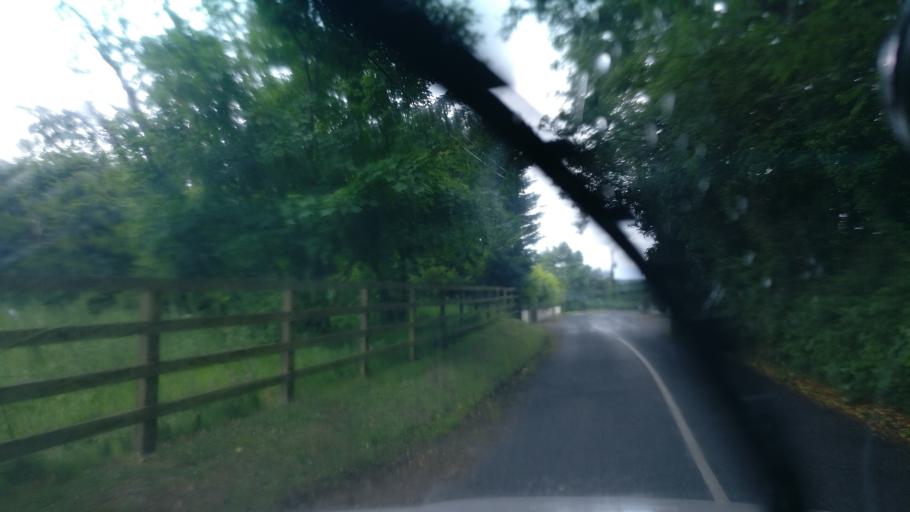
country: IE
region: Connaught
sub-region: County Galway
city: Loughrea
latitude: 53.1750
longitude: -8.5658
